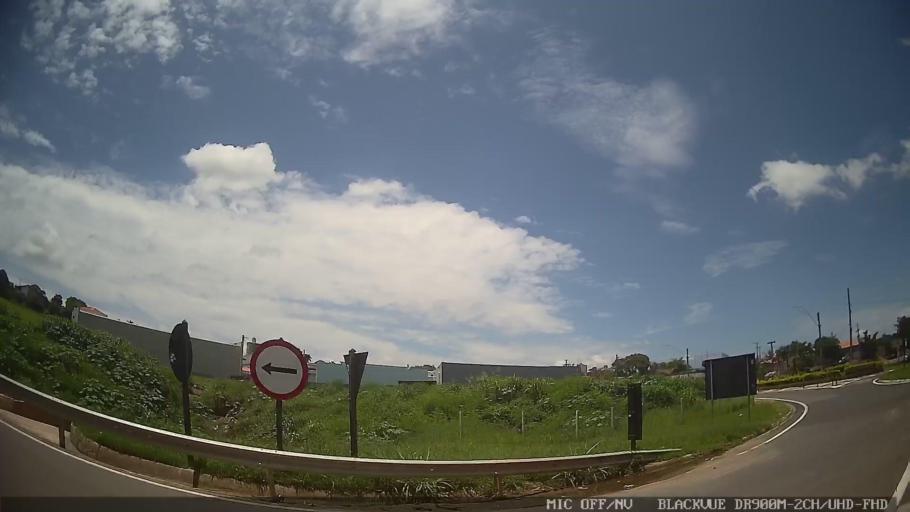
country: BR
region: Sao Paulo
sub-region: Laranjal Paulista
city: Laranjal Paulista
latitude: -23.0411
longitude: -47.8404
